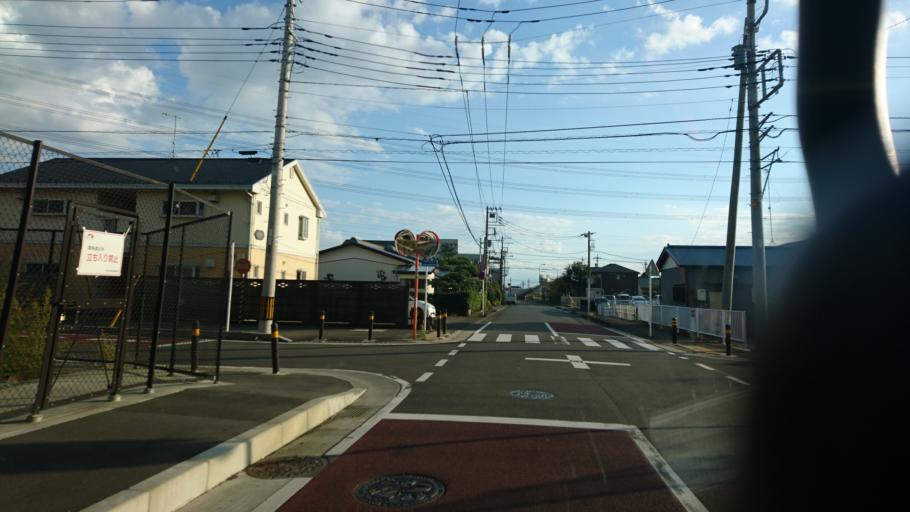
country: JP
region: Kanagawa
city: Atsugi
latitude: 35.4065
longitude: 139.3585
